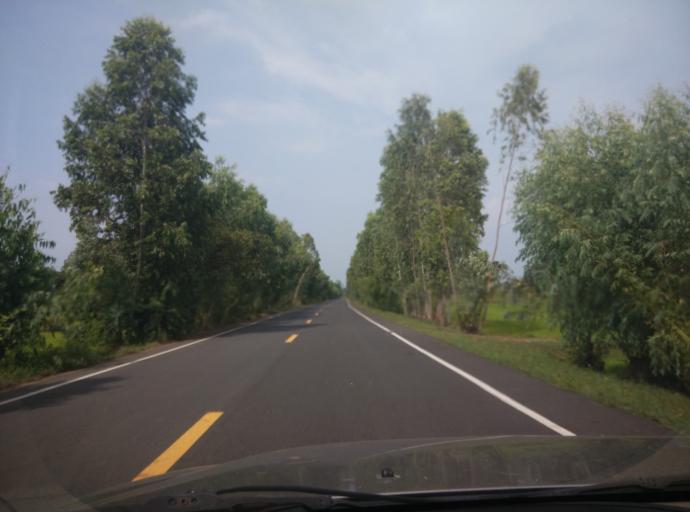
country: TH
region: Sisaket
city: Huai Thap Than
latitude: 15.0400
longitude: 104.0807
